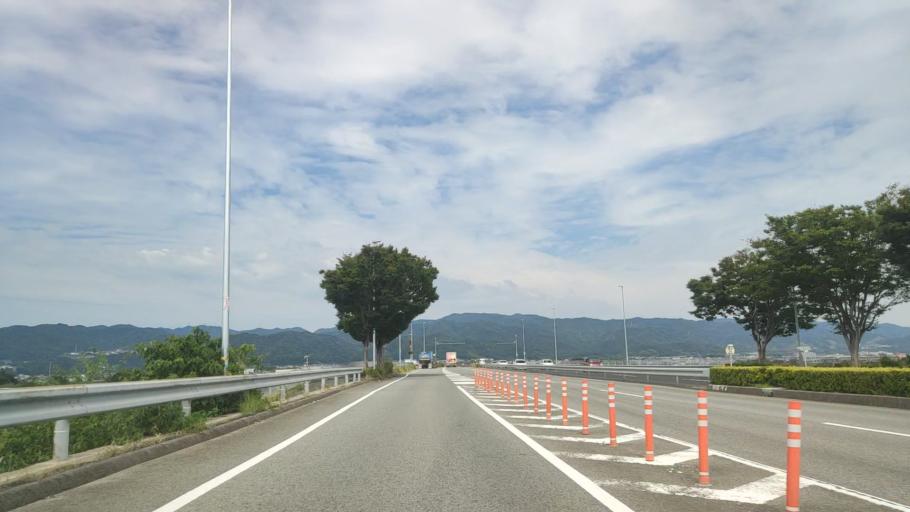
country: JP
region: Wakayama
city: Wakayama-shi
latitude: 34.2471
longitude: 135.2182
